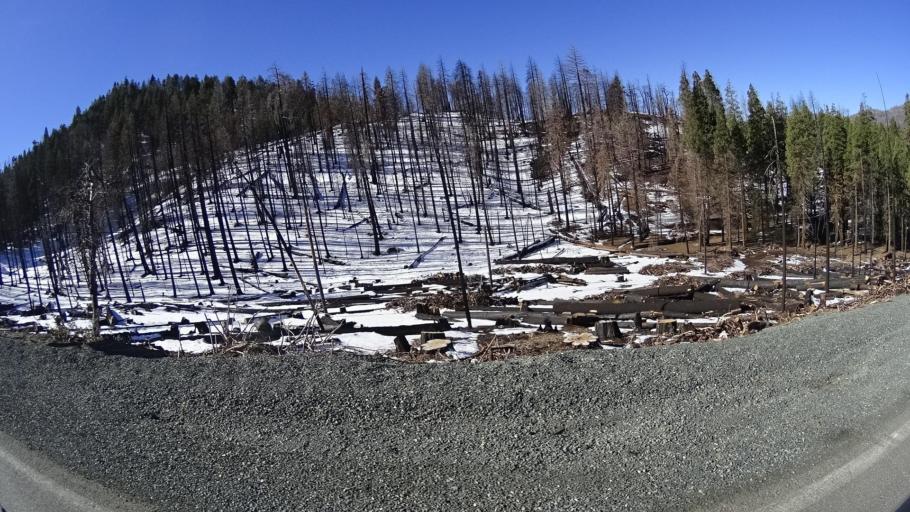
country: US
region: California
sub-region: Kern County
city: Alta Sierra
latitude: 35.7401
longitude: -118.5567
